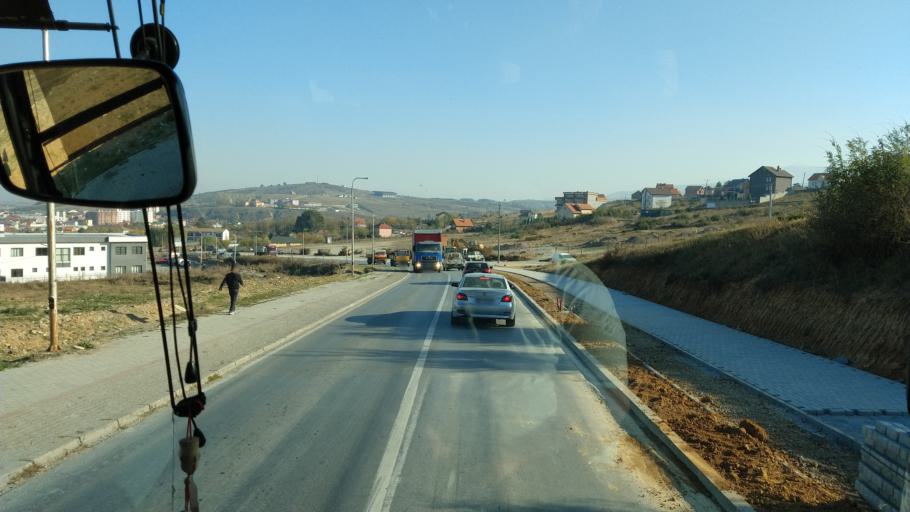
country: XK
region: Ferizaj
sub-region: Komuna e Shtimes
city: Shtime
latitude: 42.4369
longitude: 21.0235
